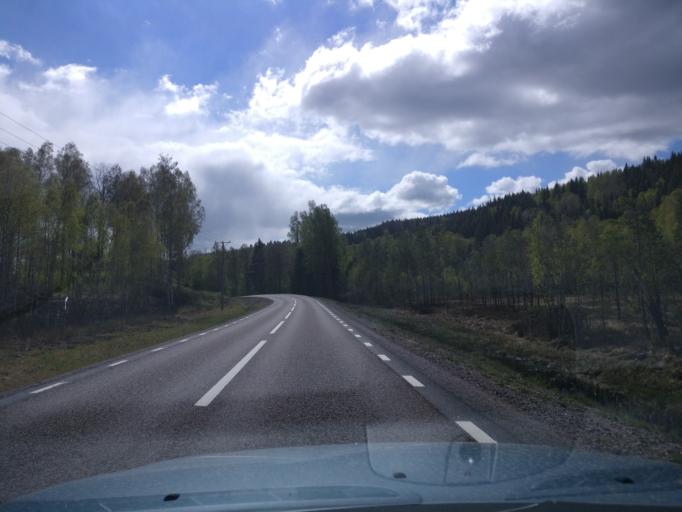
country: SE
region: Vaermland
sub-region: Hagfors Kommun
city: Hagfors
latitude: 59.8997
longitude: 13.6763
